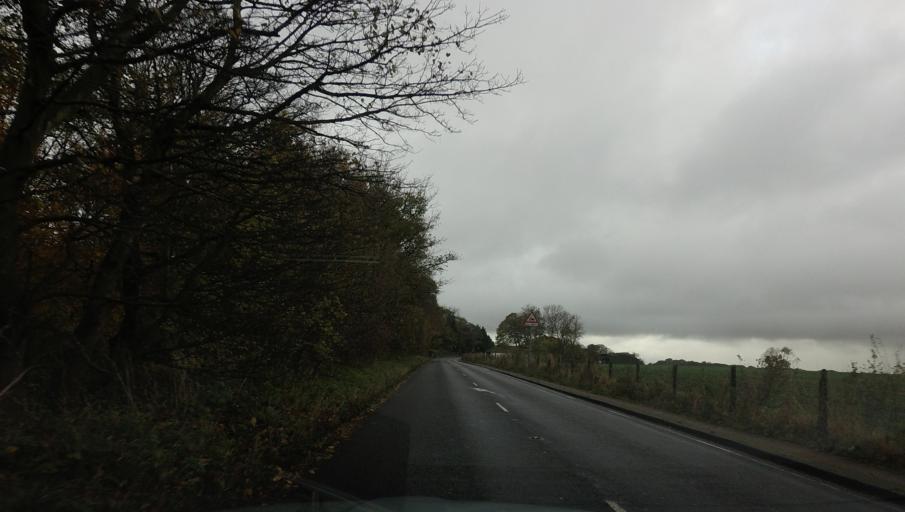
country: GB
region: Scotland
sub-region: Fife
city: East Wemyss
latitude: 56.1453
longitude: -3.1012
